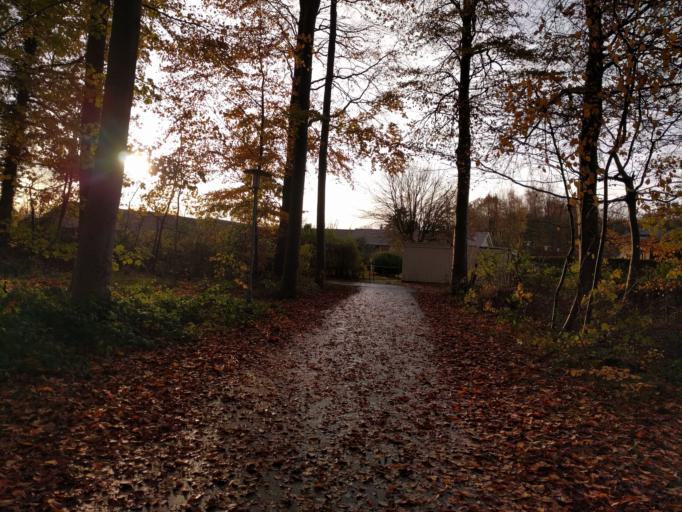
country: DK
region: South Denmark
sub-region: Fredericia Kommune
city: Snoghoj
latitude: 55.5334
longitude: 9.7252
